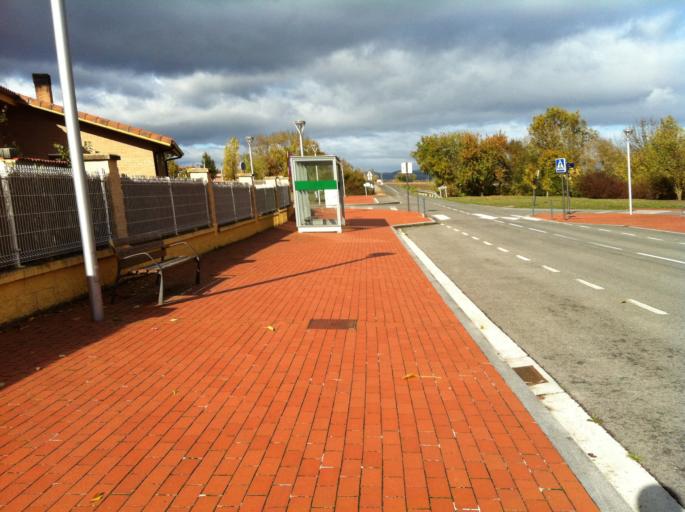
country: ES
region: Basque Country
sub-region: Provincia de Alava
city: Gasteiz / Vitoria
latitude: 42.8205
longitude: -2.6918
